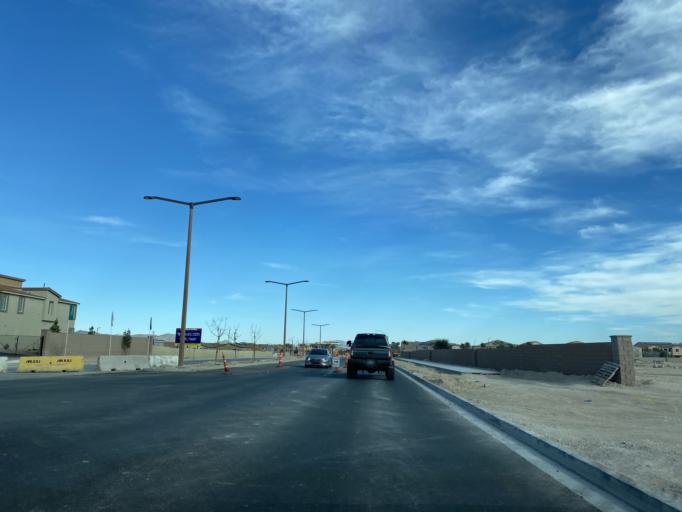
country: US
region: Nevada
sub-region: Clark County
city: North Las Vegas
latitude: 36.2912
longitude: -115.2006
